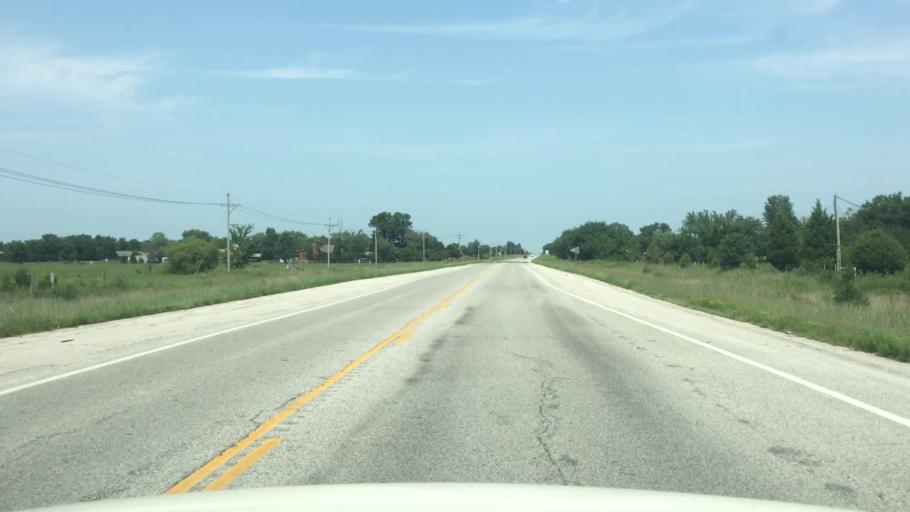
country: US
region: Kansas
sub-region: Cherokee County
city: Galena
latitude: 37.0903
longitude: -94.7043
